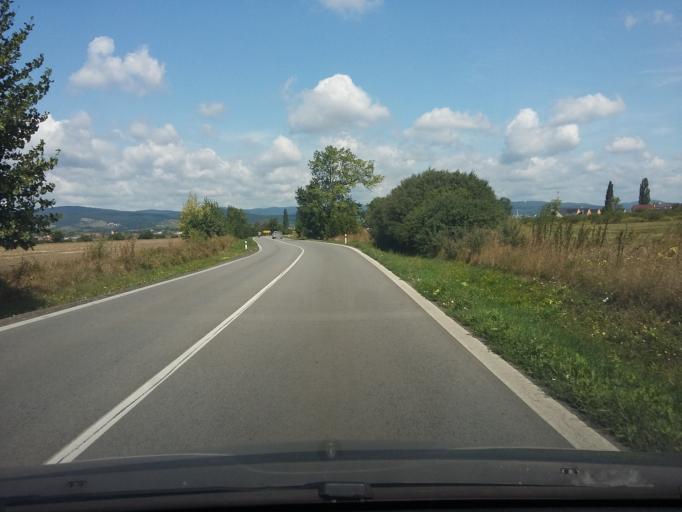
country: SK
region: Bratislavsky
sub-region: Okres Pezinok
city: Pezinok
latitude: 48.2522
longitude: 17.2615
